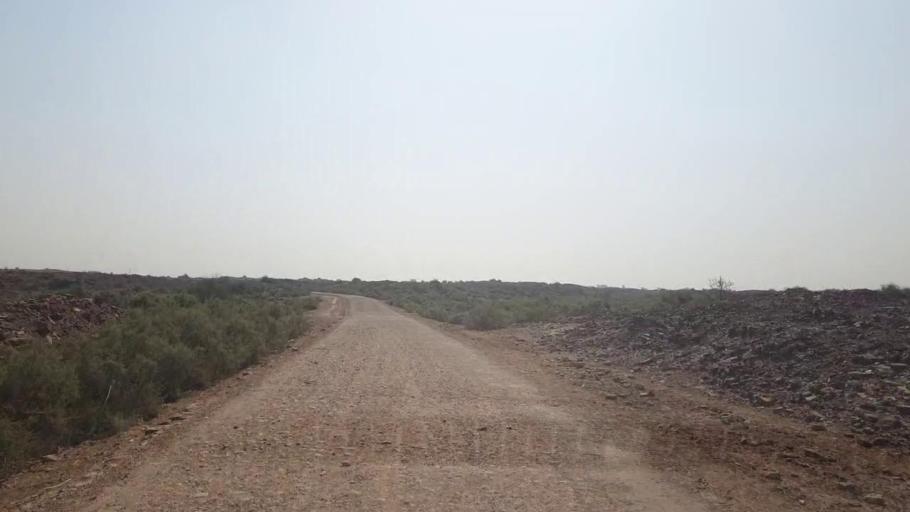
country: PK
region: Sindh
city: Berani
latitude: 25.8827
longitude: 68.7707
